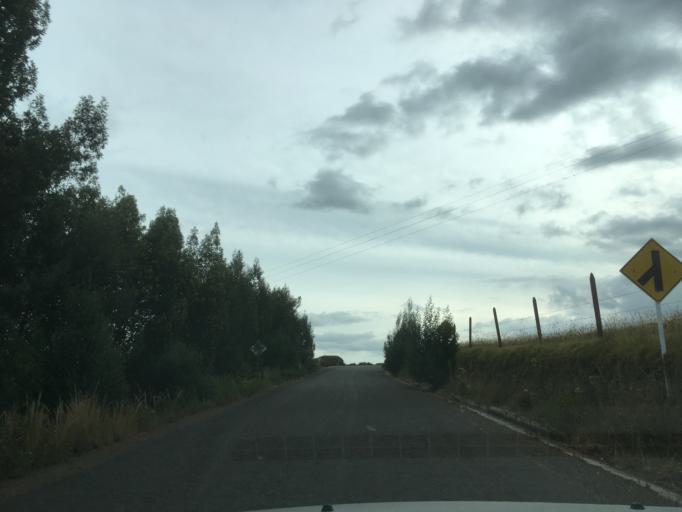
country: CO
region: Boyaca
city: Firavitoba
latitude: 5.6807
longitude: -73.0330
